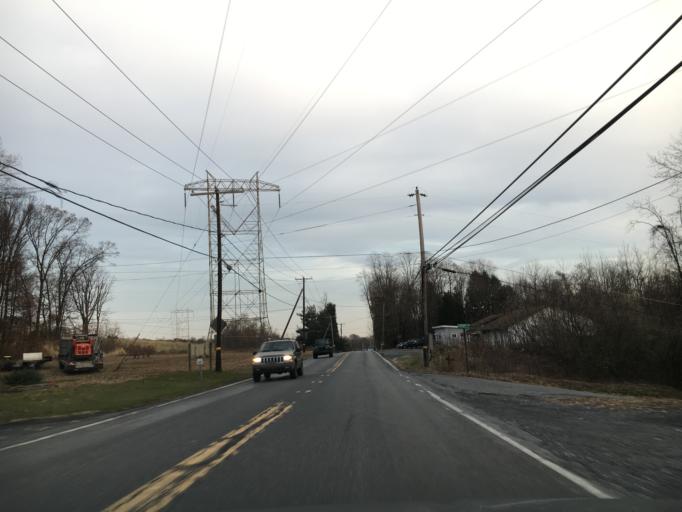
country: US
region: Pennsylvania
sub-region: Lehigh County
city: Slatington
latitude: 40.7188
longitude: -75.6053
